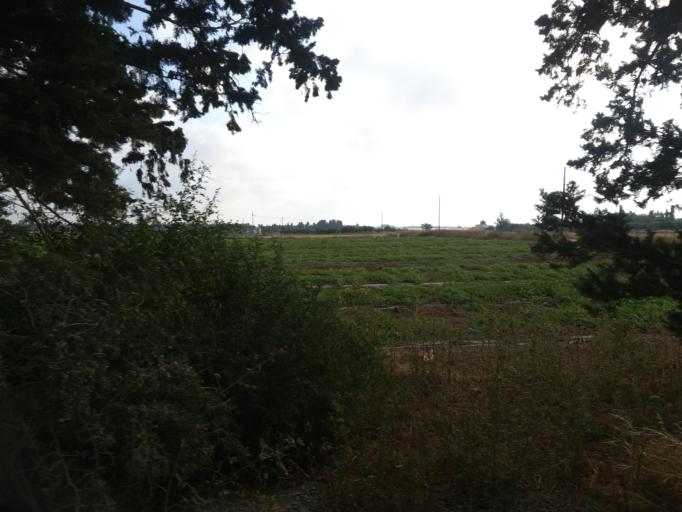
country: CY
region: Larnaka
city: Meneou
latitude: 34.8451
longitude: 33.5977
